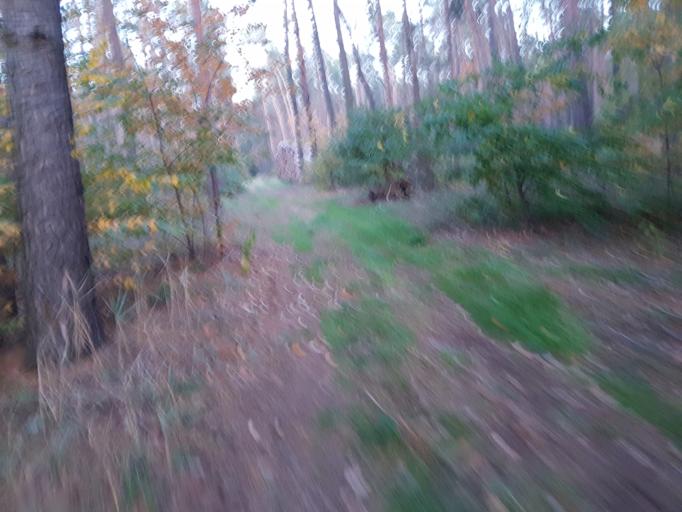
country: DE
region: Brandenburg
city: Bad Liebenwerda
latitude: 51.5426
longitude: 13.3783
